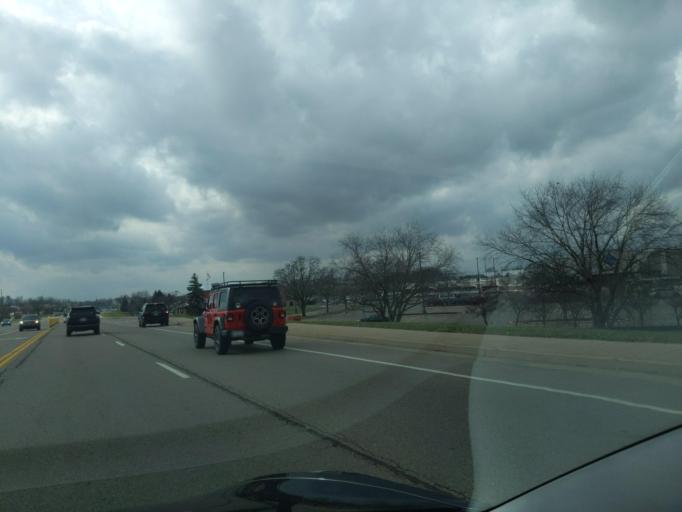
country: US
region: Kentucky
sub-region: Boone County
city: Florence
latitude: 39.0151
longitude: -84.6369
